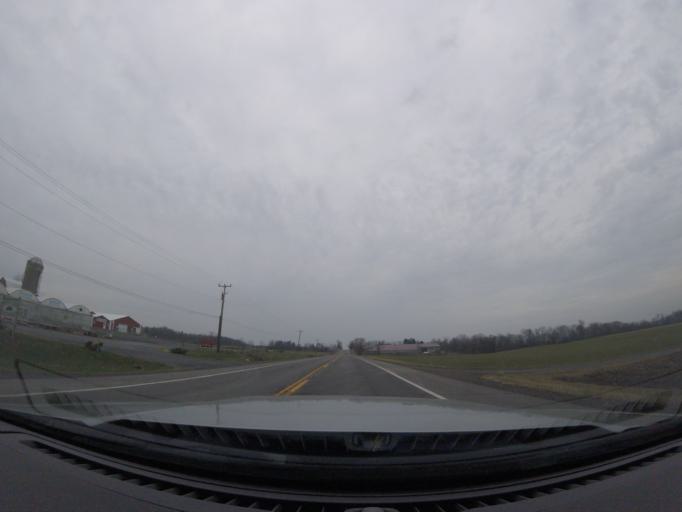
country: US
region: New York
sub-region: Yates County
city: Penn Yan
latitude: 42.6444
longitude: -76.9436
